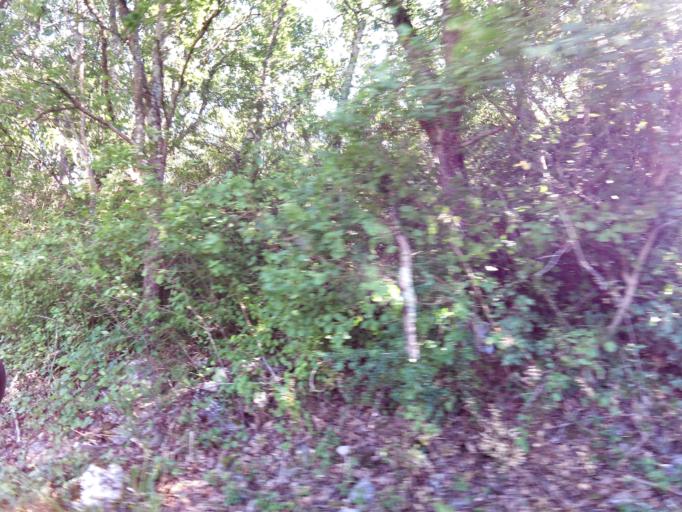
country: FR
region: Languedoc-Roussillon
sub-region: Departement du Gard
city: Quissac
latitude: 43.8790
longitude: 4.0343
